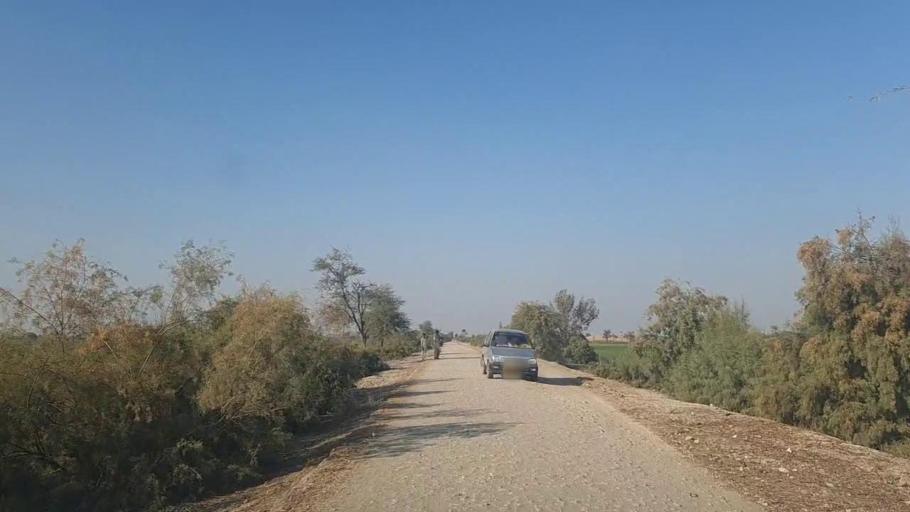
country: PK
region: Sindh
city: Jam Sahib
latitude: 26.3261
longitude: 68.7145
